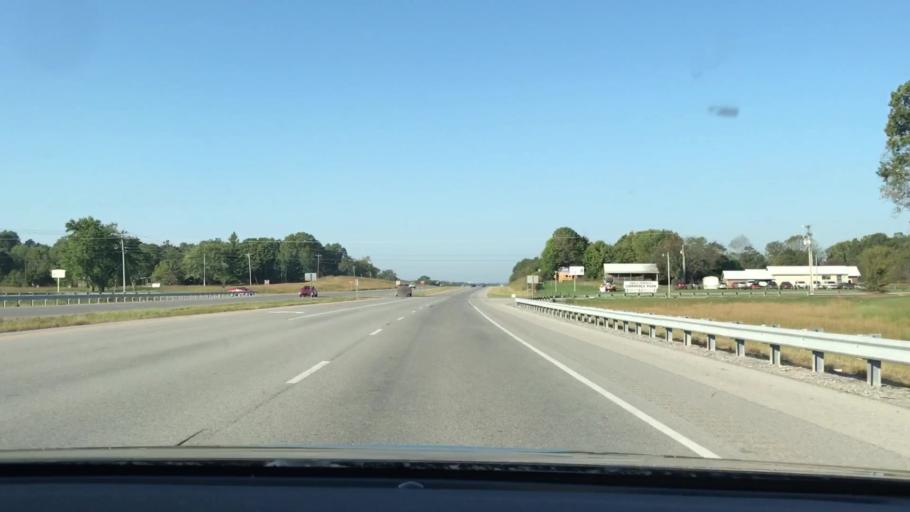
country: US
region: Kentucky
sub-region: Trigg County
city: Cadiz
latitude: 36.8718
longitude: -87.7639
